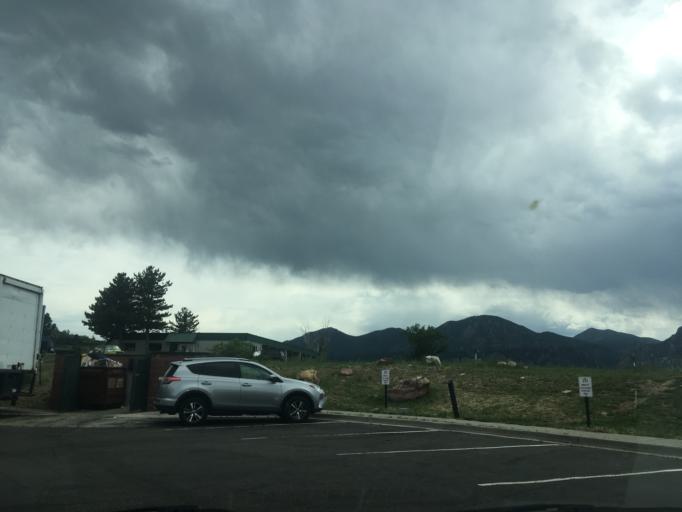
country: US
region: Colorado
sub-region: Boulder County
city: Superior
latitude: 39.9537
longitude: -105.2329
